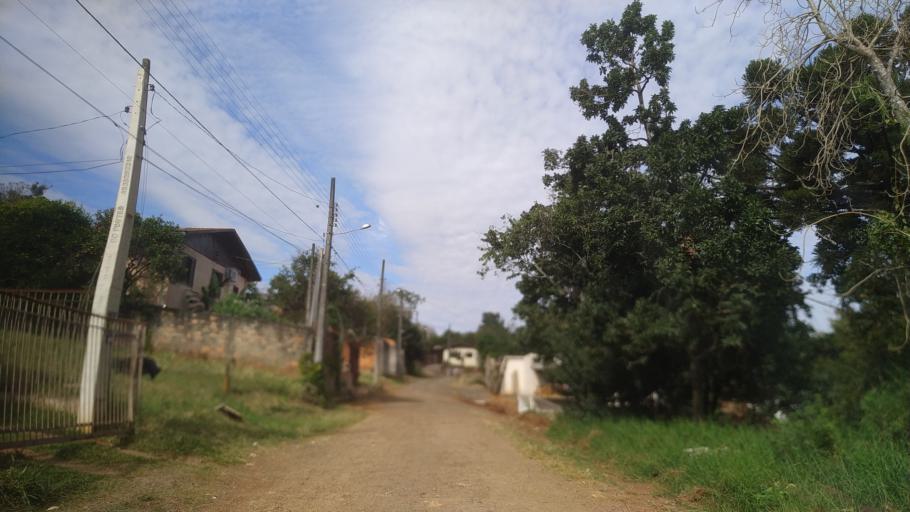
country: BR
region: Santa Catarina
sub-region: Chapeco
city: Chapeco
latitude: -27.1081
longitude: -52.6015
